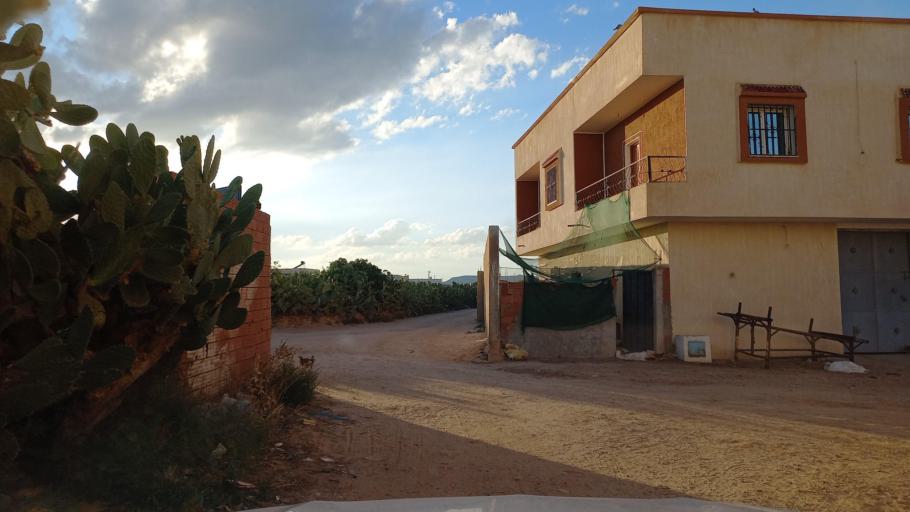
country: TN
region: Al Qasrayn
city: Sbiba
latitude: 35.3795
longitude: 9.0532
